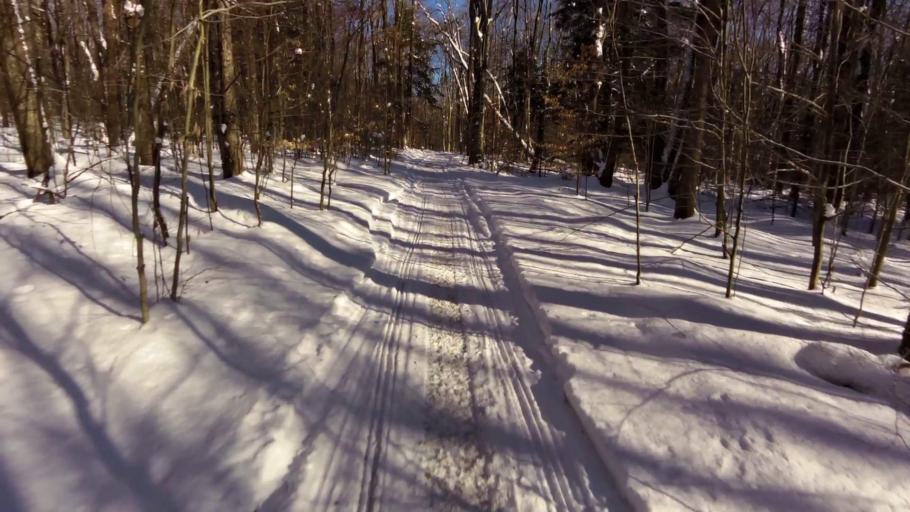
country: US
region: New York
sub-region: Cattaraugus County
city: Salamanca
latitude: 42.0274
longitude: -78.7829
